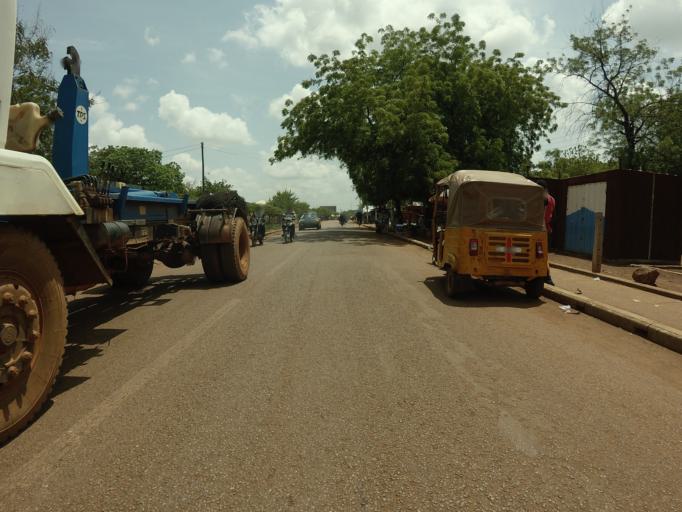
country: GH
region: Northern
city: Tamale
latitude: 9.4015
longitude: -0.8493
